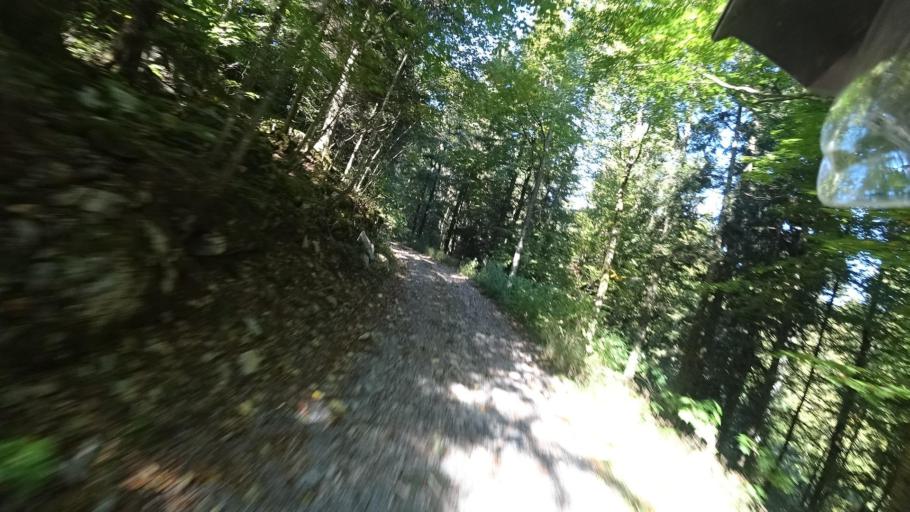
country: HR
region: Primorsko-Goranska
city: Vrbovsko
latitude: 45.2726
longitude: 15.1029
